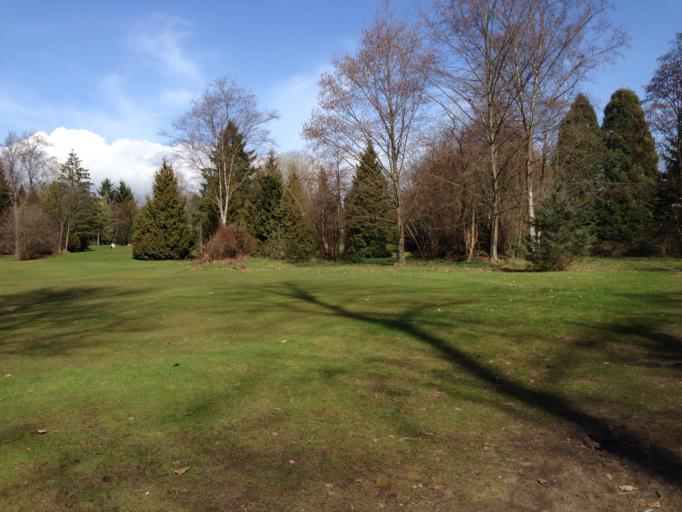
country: CA
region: British Columbia
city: Burnaby
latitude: 49.2773
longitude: -122.9804
